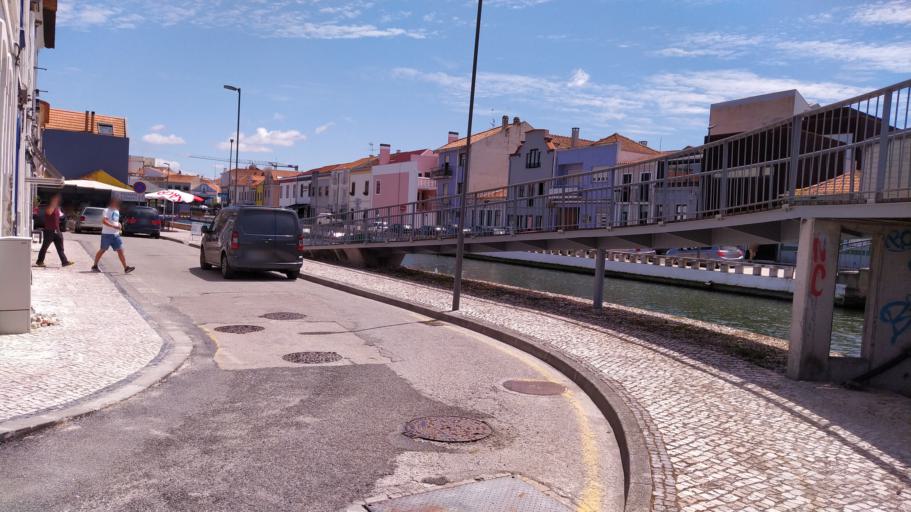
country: PT
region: Aveiro
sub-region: Aveiro
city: Aveiro
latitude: 40.6441
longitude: -8.6562
